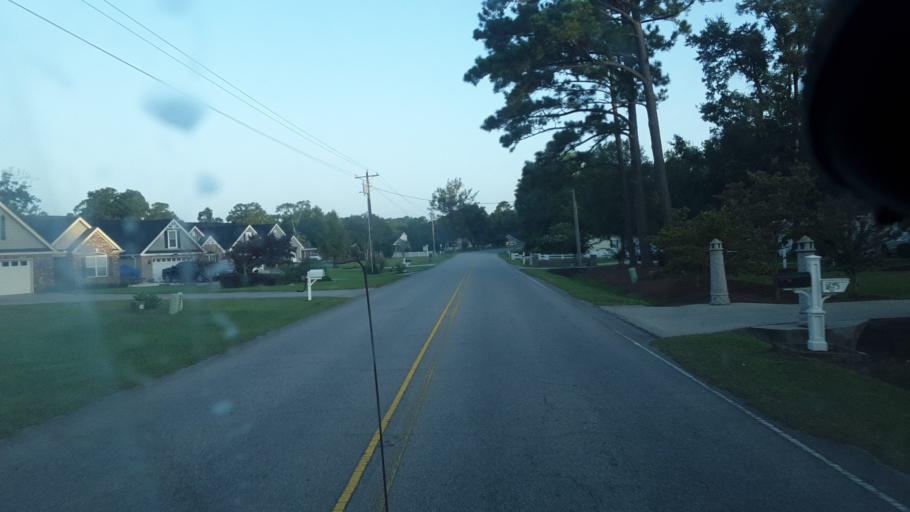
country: US
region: North Carolina
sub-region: Brunswick County
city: Calabash
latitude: 33.8824
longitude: -78.5463
